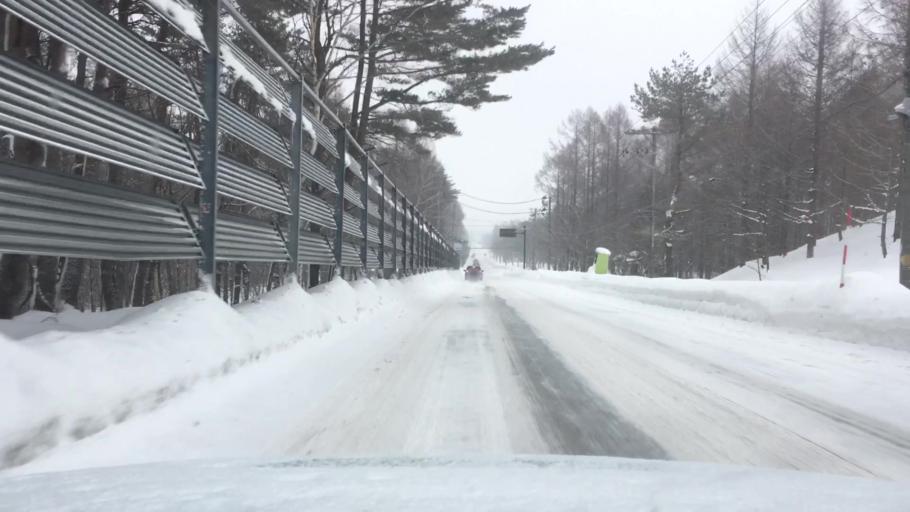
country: JP
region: Akita
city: Hanawa
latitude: 40.0055
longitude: 140.9721
